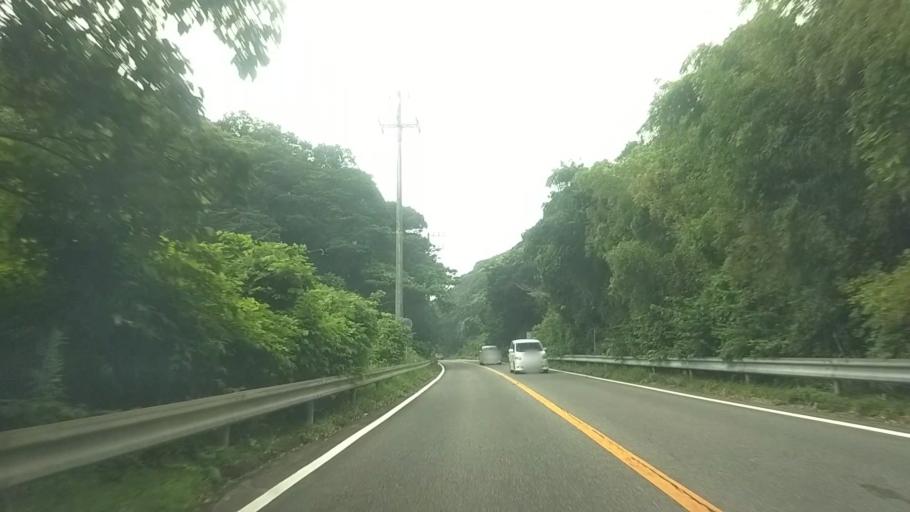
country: JP
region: Chiba
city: Katsuura
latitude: 35.1574
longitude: 140.3096
